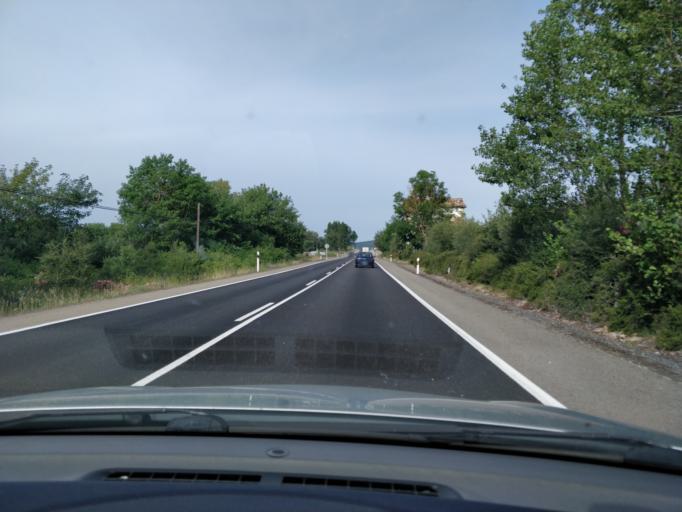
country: ES
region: Castille and Leon
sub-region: Provincia de Burgos
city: Medina de Pomar
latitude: 42.9309
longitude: -3.5354
